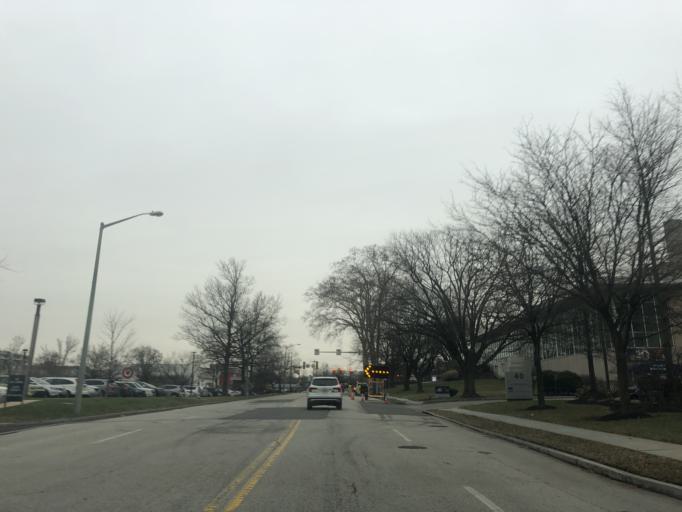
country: US
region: Pennsylvania
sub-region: Montgomery County
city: Bala-Cynwyd
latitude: 40.0085
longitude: -75.2149
